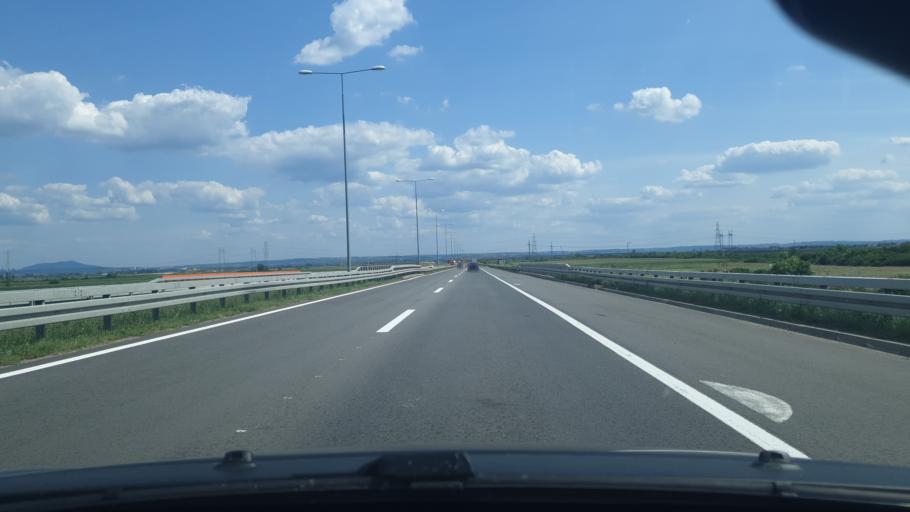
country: RS
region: Central Serbia
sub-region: Belgrade
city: Surcin
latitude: 44.7840
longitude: 20.2623
